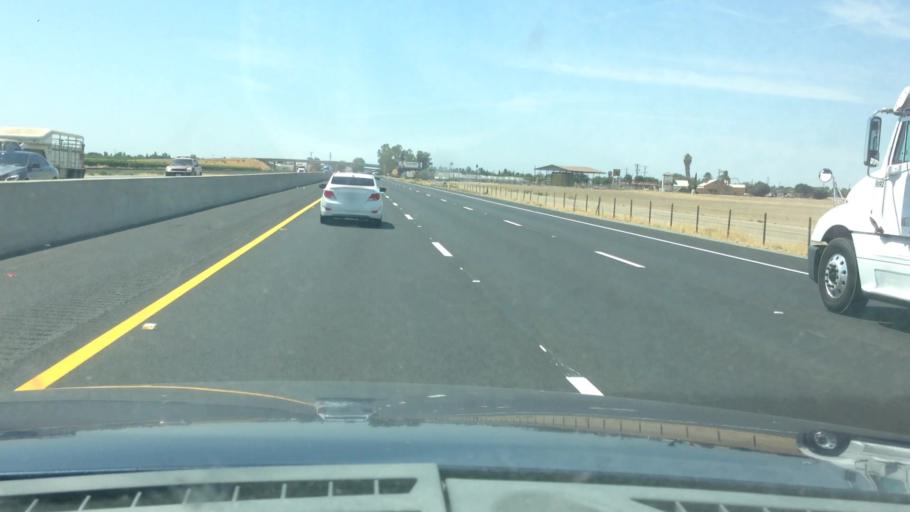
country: US
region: California
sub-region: Kern County
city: McFarland
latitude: 35.6964
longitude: -119.2317
